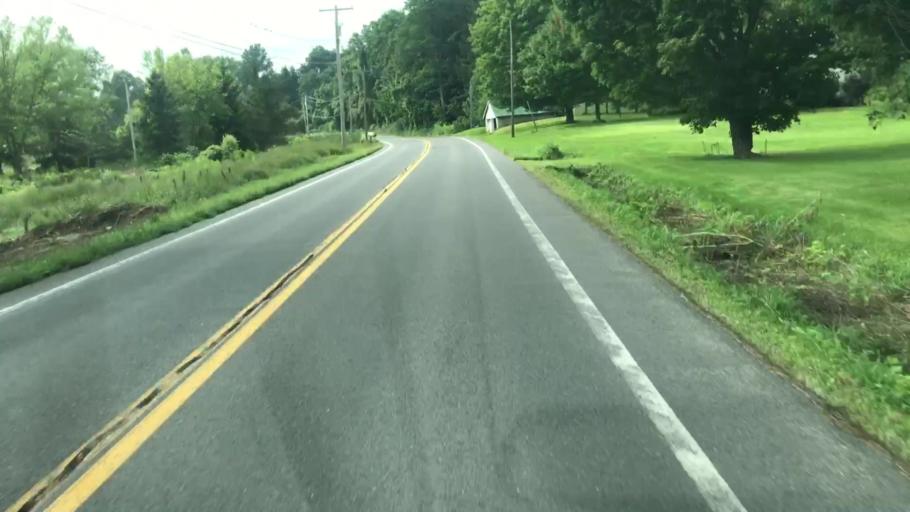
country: US
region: New York
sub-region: Onondaga County
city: Peru
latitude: 43.0568
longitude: -76.3656
